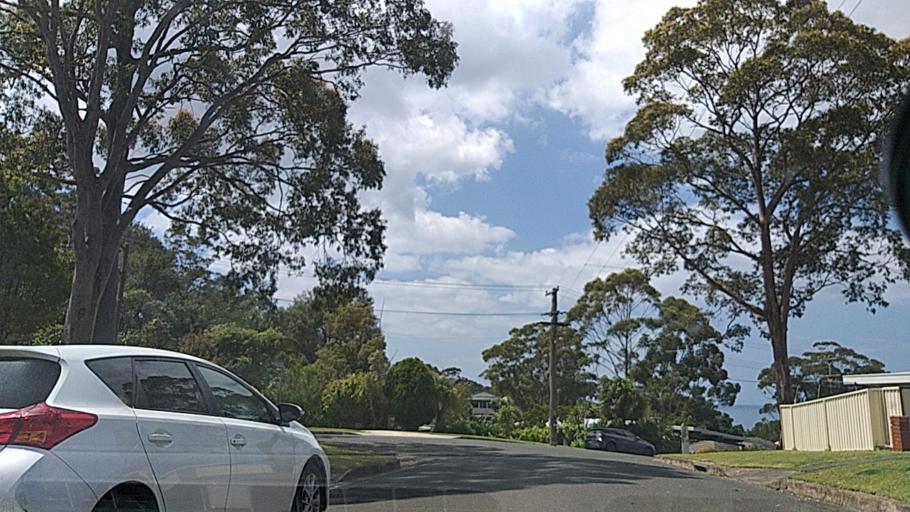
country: AU
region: New South Wales
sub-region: Wollongong
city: Bulli
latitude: -34.3143
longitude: 150.9134
